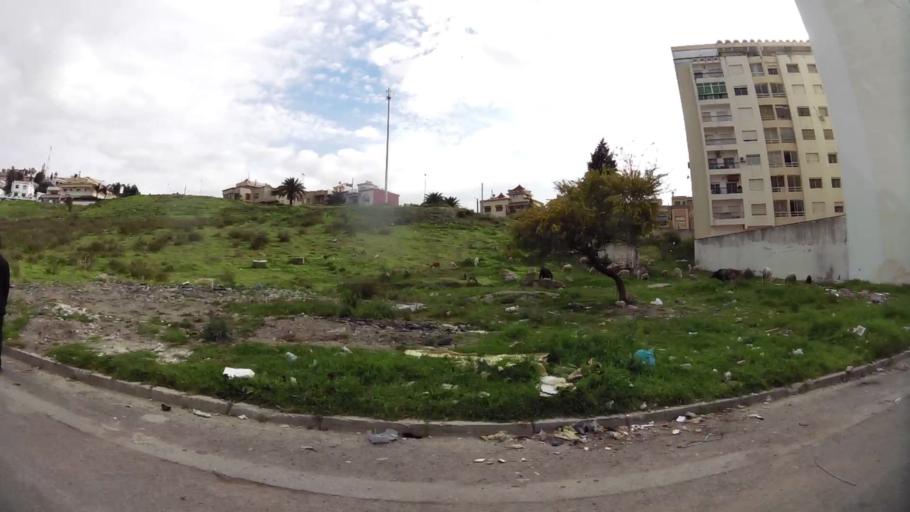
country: MA
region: Tanger-Tetouan
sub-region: Tanger-Assilah
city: Tangier
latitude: 35.7706
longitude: -5.7929
